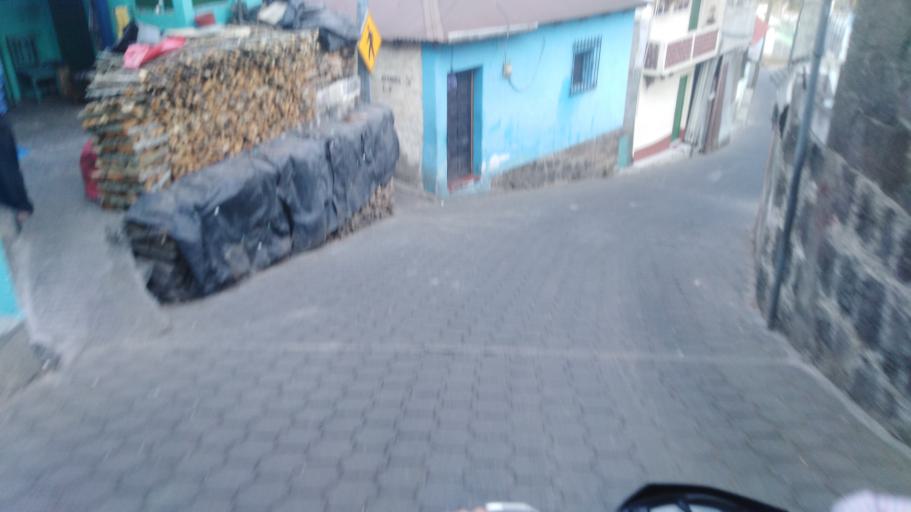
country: GT
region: Solola
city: San Pedro La Laguna
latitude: 14.6908
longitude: -91.2706
